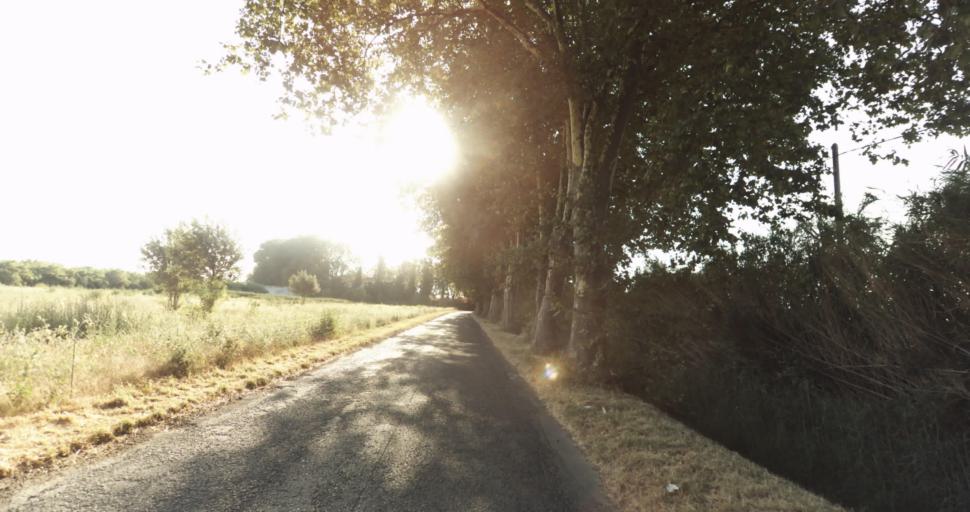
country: FR
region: Languedoc-Roussillon
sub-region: Departement des Pyrenees-Orientales
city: Latour-Bas-Elne
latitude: 42.5961
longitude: 3.0208
